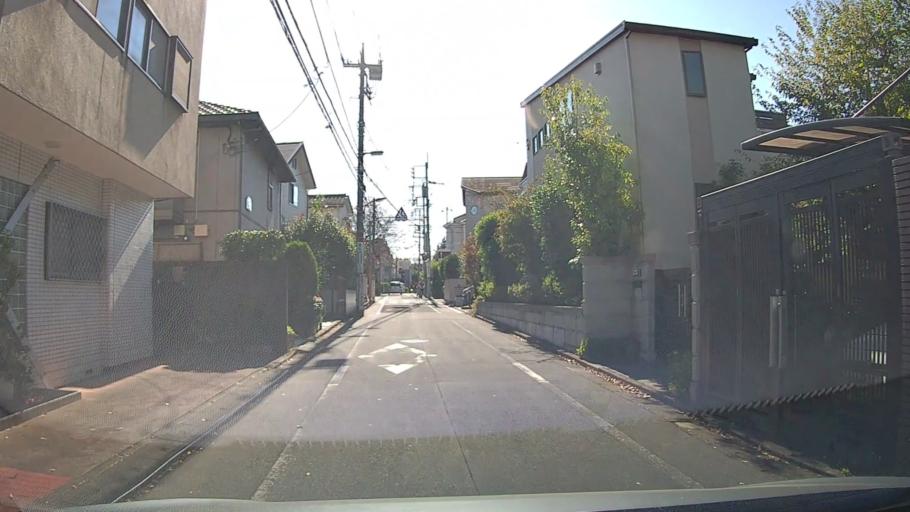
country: JP
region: Saitama
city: Wako
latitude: 35.7387
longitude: 139.6089
